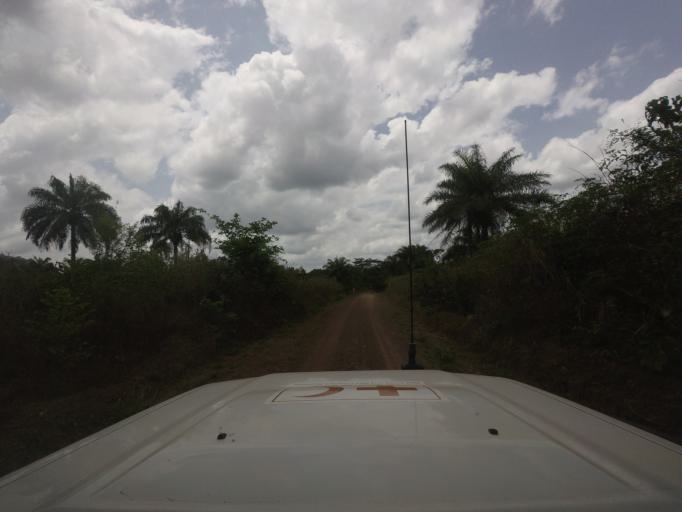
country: GN
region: Nzerekore
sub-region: Yomou
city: Yomou
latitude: 7.2690
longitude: -9.1853
